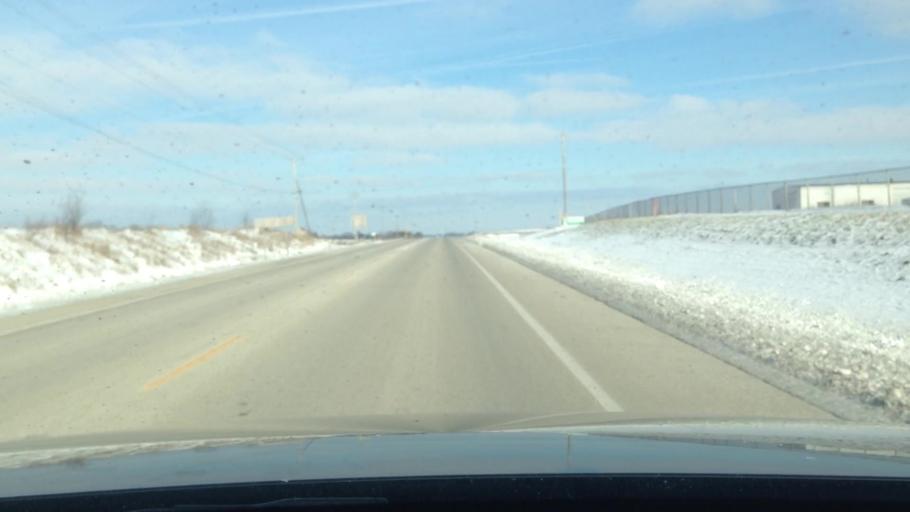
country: US
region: Wisconsin
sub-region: Walworth County
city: East Troy
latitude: 42.6932
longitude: -88.4047
